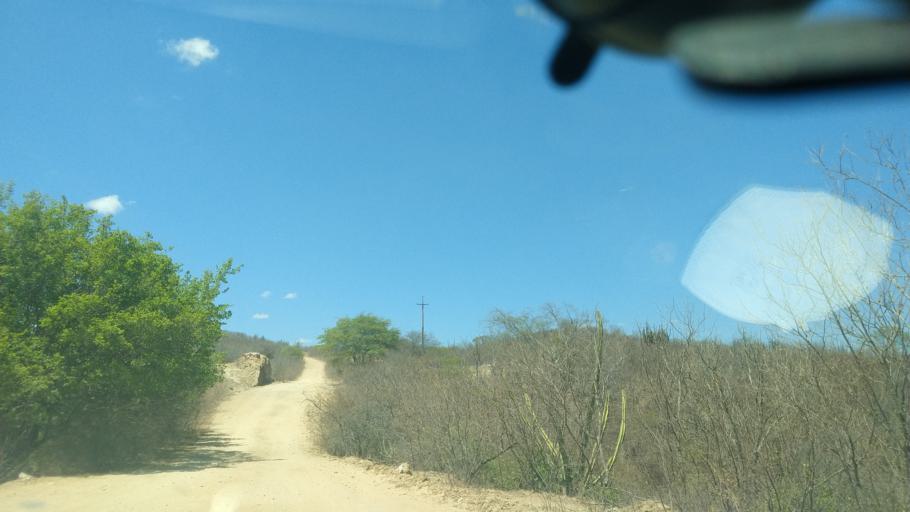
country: BR
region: Rio Grande do Norte
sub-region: Cerro Cora
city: Cerro Cora
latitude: -6.0120
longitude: -36.2979
